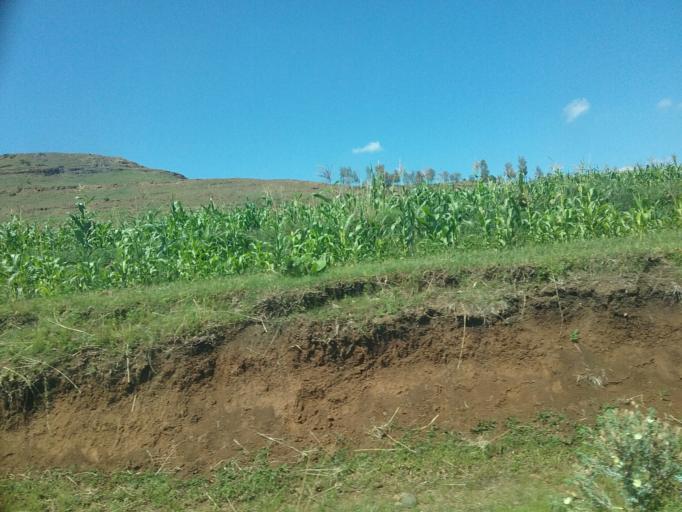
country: LS
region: Berea
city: Teyateyaneng
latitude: -29.2156
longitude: 27.8630
